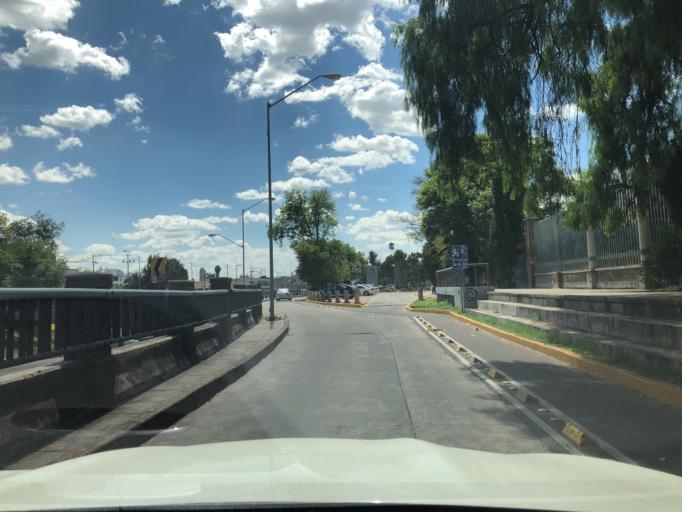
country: MX
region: Aguascalientes
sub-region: Aguascalientes
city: Aguascalientes
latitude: 21.8835
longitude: -102.2775
